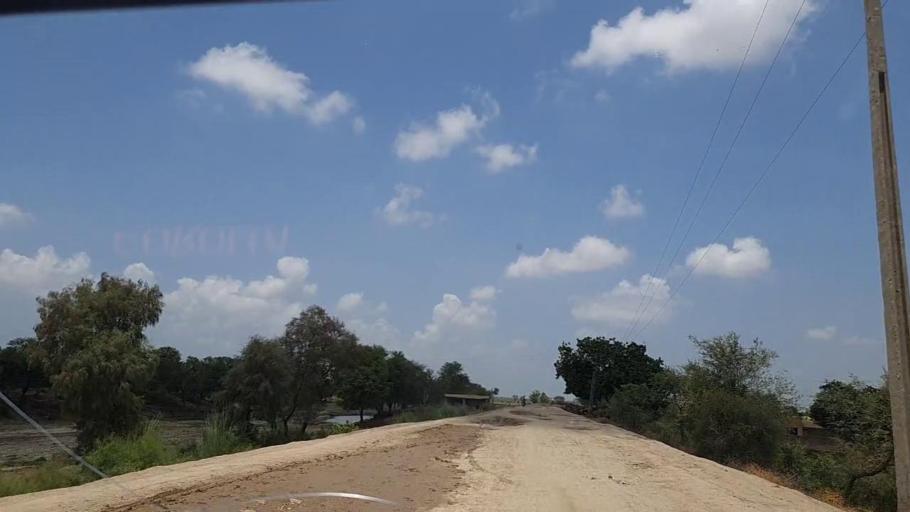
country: PK
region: Sindh
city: Tharu Shah
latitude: 26.9276
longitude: 67.9900
